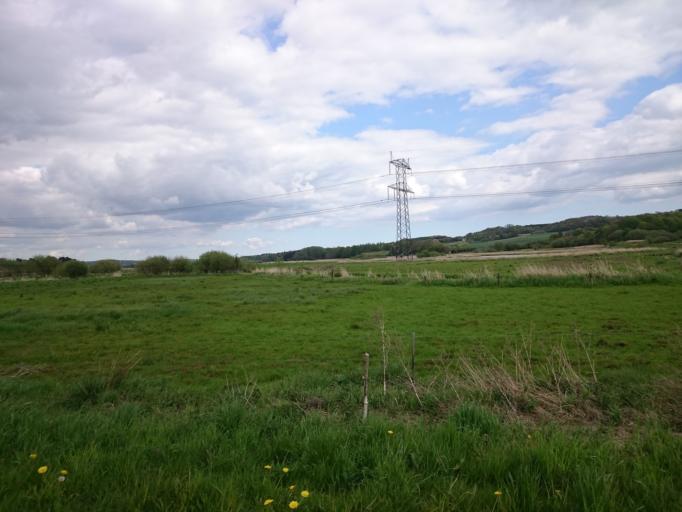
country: DK
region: Central Jutland
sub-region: Arhus Kommune
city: Framlev
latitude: 56.1331
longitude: 10.0404
